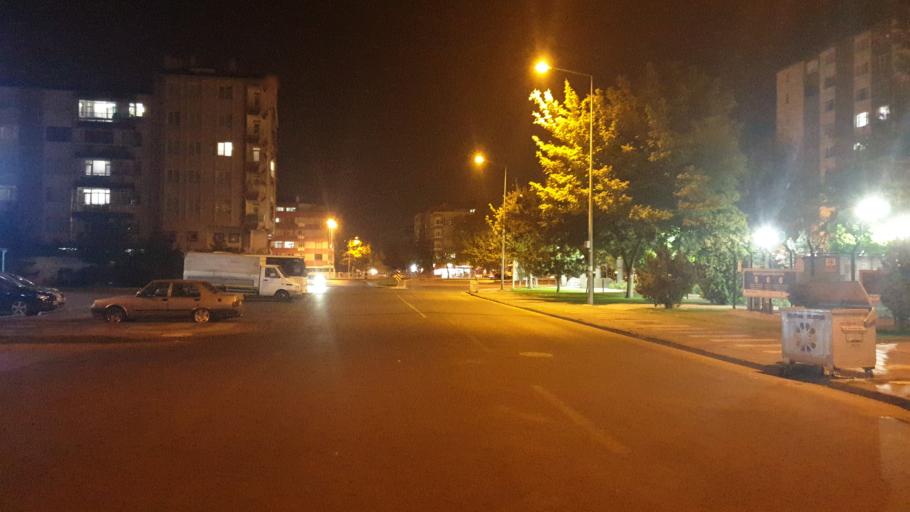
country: TR
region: Kayseri
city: Kayseri
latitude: 38.7295
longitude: 35.4942
